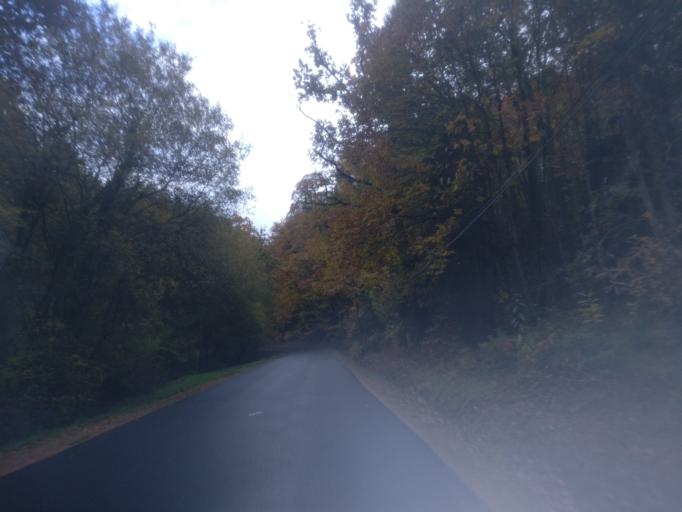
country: FR
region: Brittany
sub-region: Departement d'Ille-et-Vilaine
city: Guichen
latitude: 48.0009
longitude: -1.7887
